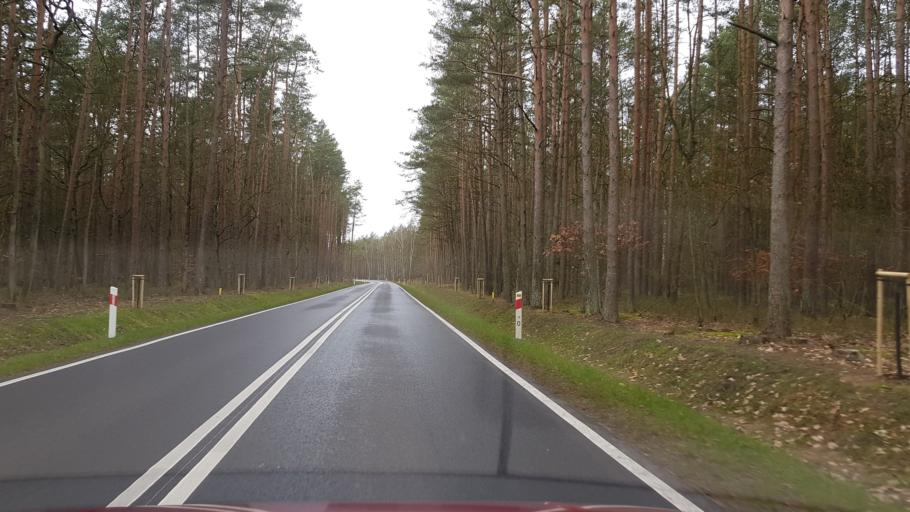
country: PL
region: West Pomeranian Voivodeship
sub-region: Powiat policki
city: Police
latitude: 53.6580
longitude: 14.4711
